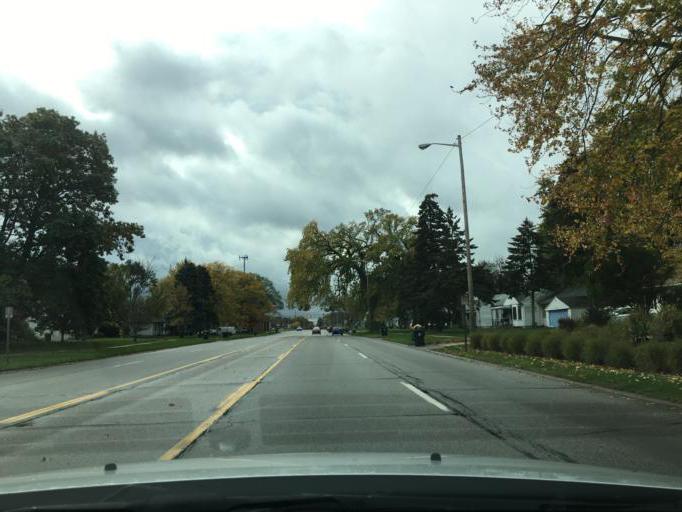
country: US
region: Michigan
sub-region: Wayne County
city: Redford
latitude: 42.3827
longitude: -83.2953
